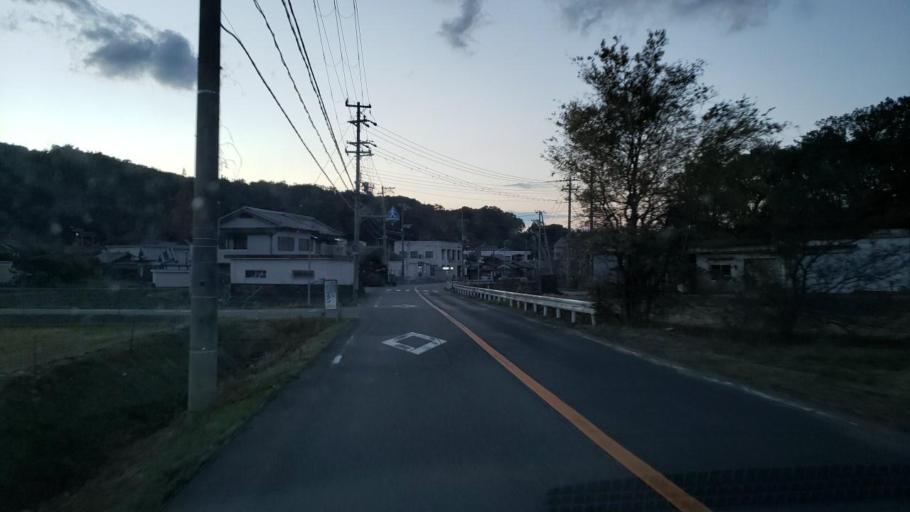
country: JP
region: Hyogo
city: Fukura
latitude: 34.2841
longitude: 134.6905
